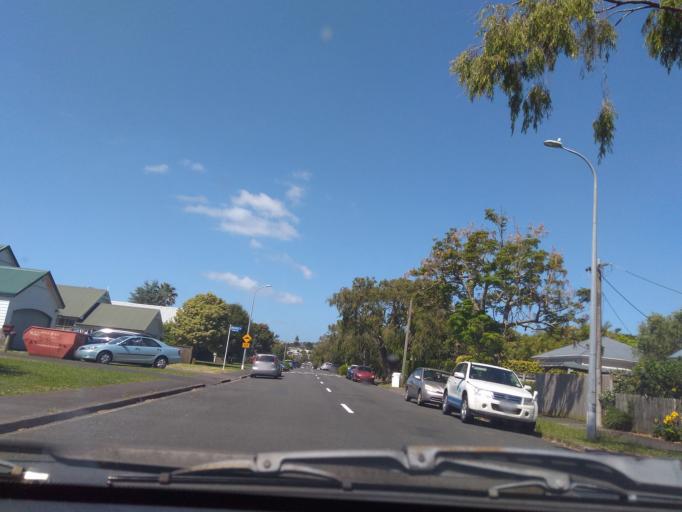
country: NZ
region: Auckland
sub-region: Auckland
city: Rosebank
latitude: -36.9006
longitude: 174.6904
